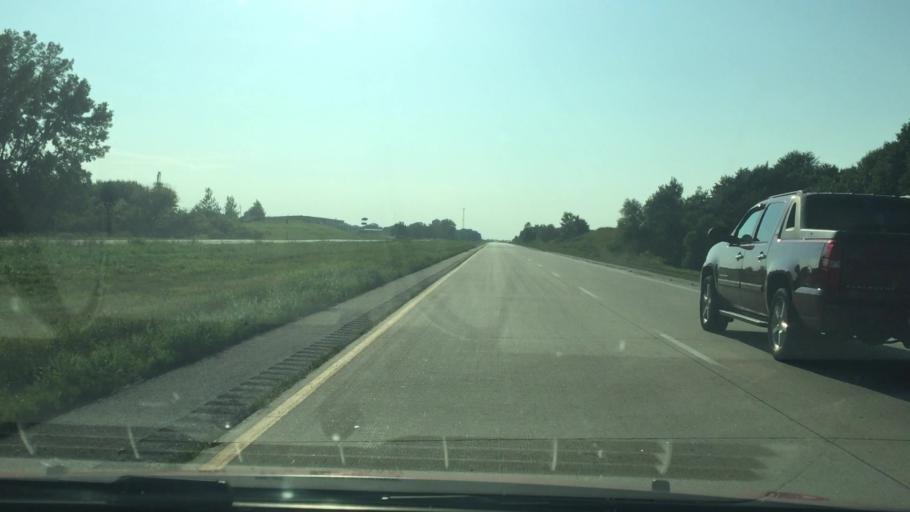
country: US
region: Iowa
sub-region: Scott County
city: Blue Grass
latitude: 41.5163
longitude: -90.8314
